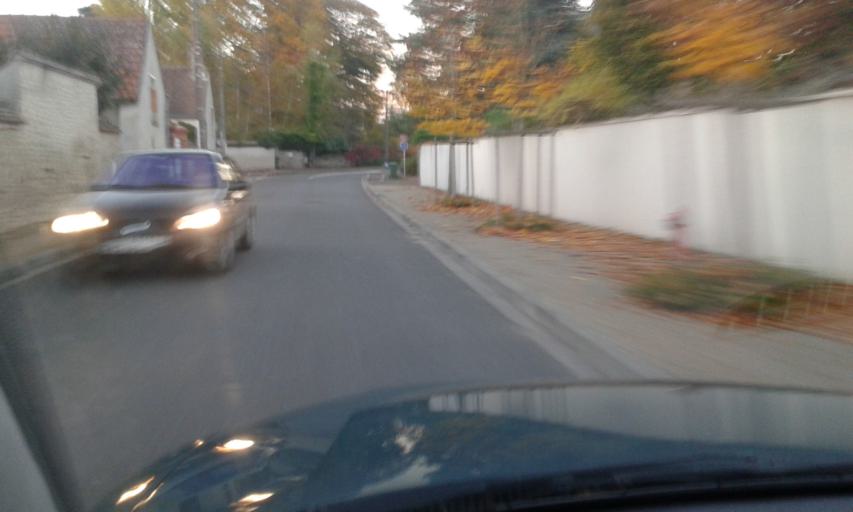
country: FR
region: Centre
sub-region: Departement du Loiret
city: Olivet
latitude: 47.8553
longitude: 1.8819
